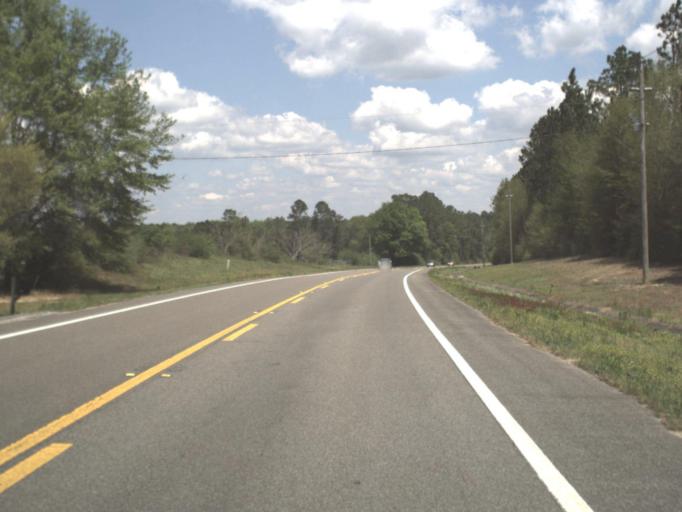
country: US
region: Florida
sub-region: Okaloosa County
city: Crestview
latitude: 30.8585
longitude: -86.6742
